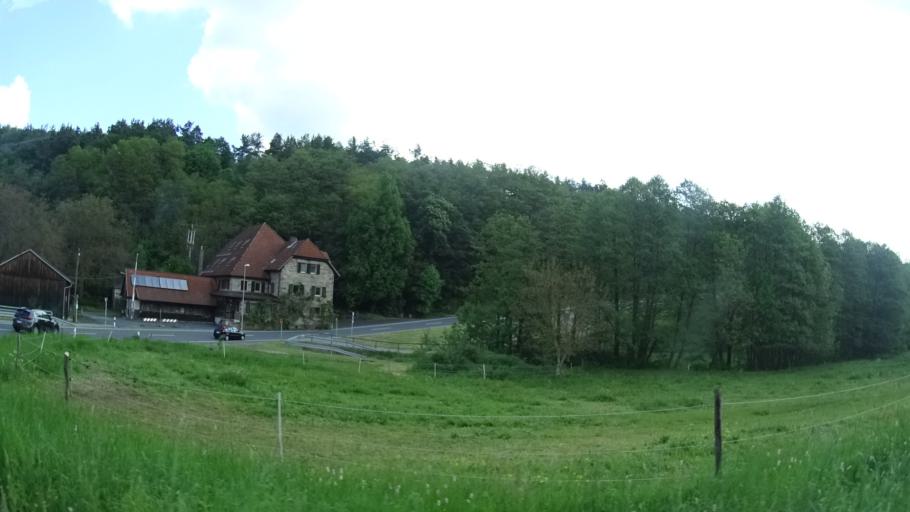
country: DE
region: Bavaria
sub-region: Regierungsbezirk Unterfranken
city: Sandberg
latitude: 50.3377
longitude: 9.9894
